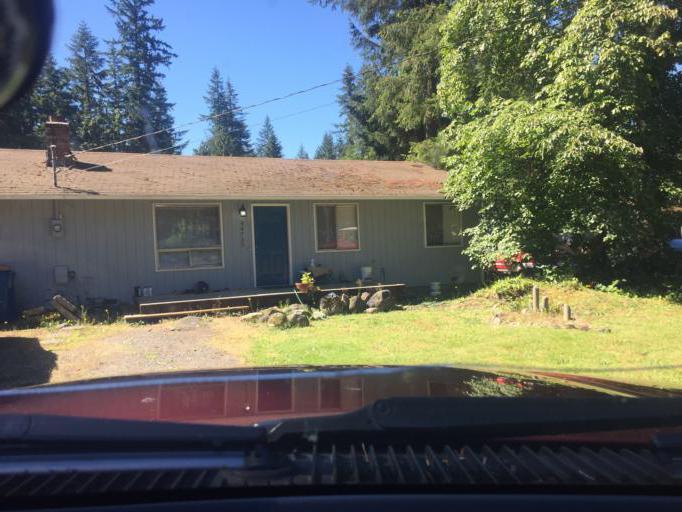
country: US
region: Washington
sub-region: King County
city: Riverbend
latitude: 47.4680
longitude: -121.7427
